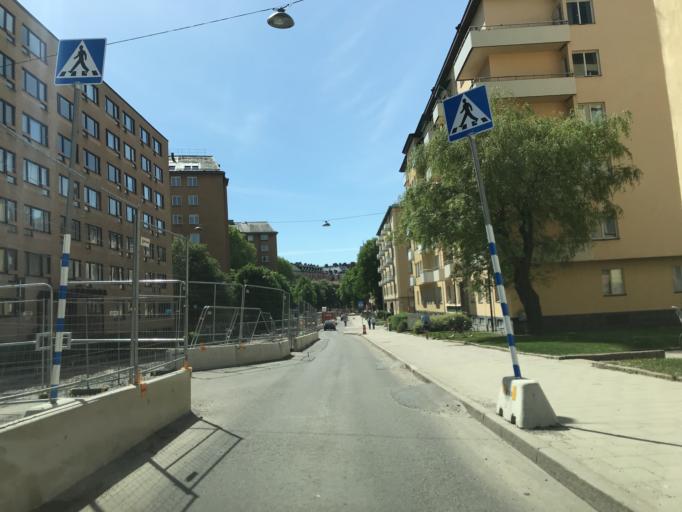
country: SE
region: Stockholm
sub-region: Stockholms Kommun
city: OEstermalm
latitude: 59.3416
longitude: 18.0968
